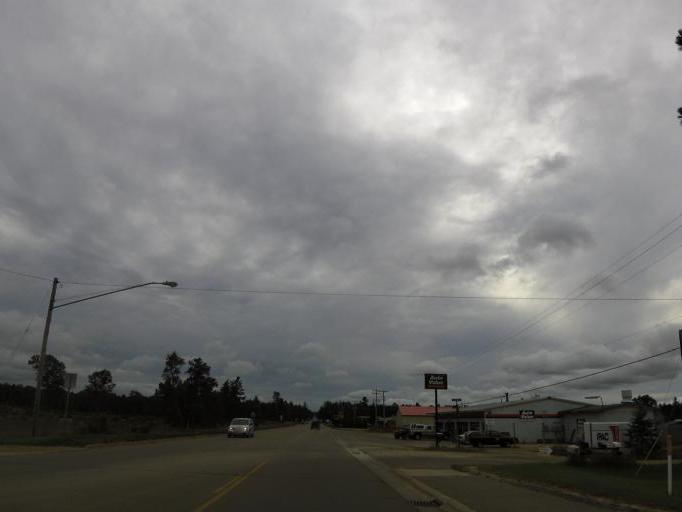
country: US
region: Michigan
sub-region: Roscommon County
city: Saint Helen
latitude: 44.3529
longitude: -84.4103
